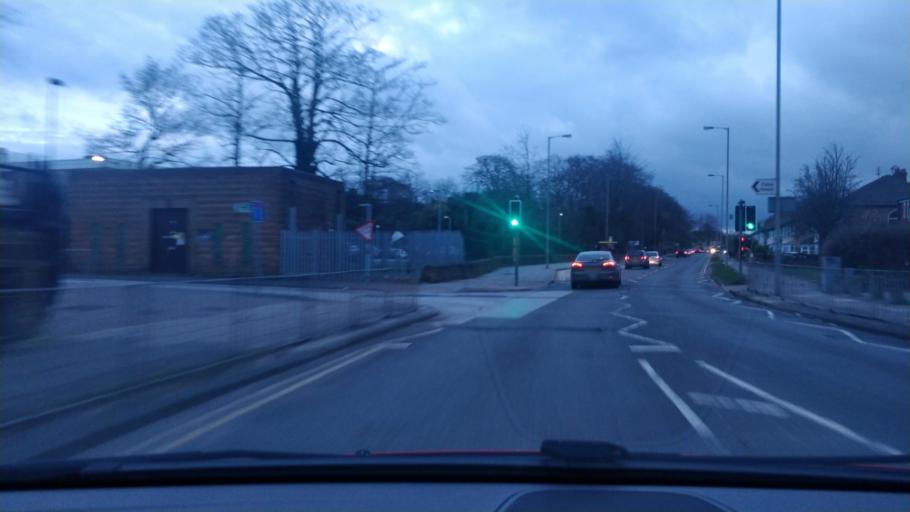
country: GB
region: England
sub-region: Knowsley
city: Knowsley
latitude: 53.4244
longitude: -2.8901
